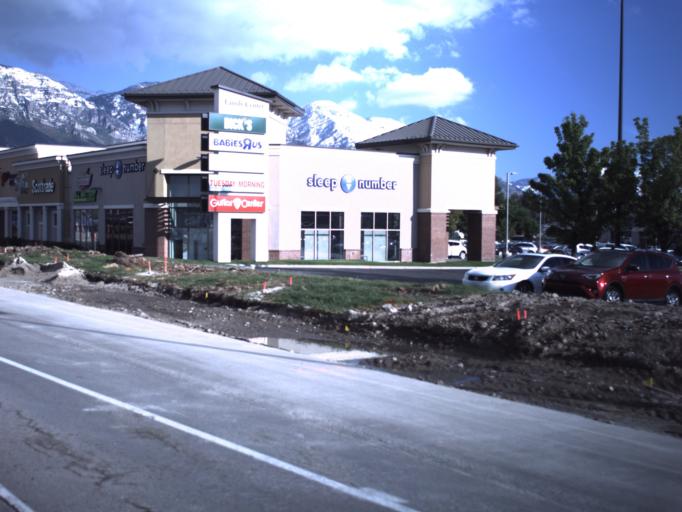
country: US
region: Utah
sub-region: Utah County
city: Orem
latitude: 40.2734
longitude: -111.6922
